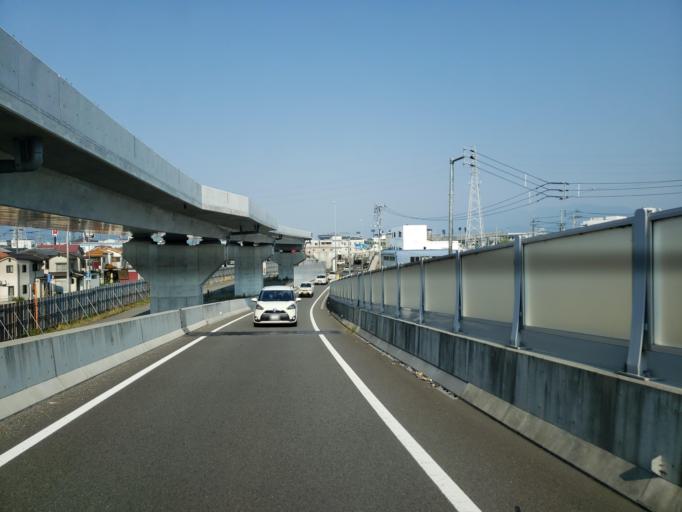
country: JP
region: Ehime
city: Masaki-cho
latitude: 33.8112
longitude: 132.7321
